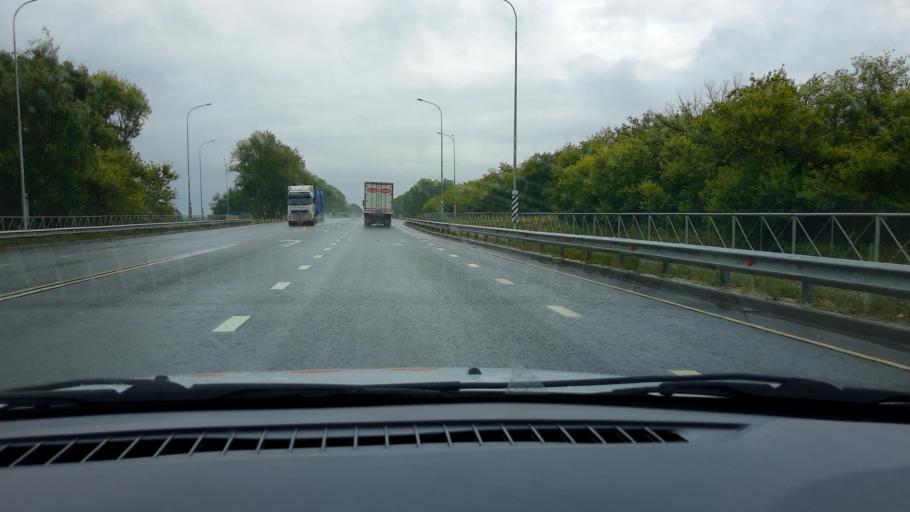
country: RU
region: Chuvashia
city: Yantikovo
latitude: 55.7898
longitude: 47.6938
